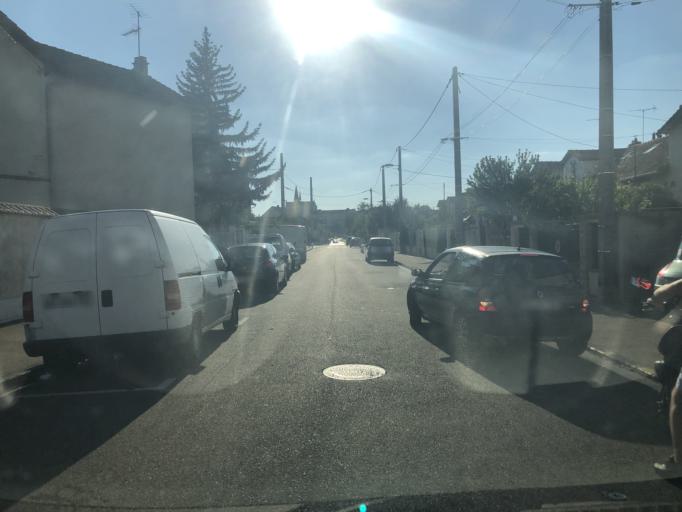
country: FR
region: Bourgogne
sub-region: Departement de l'Yonne
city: Auxerre
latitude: 47.8024
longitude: 3.5817
